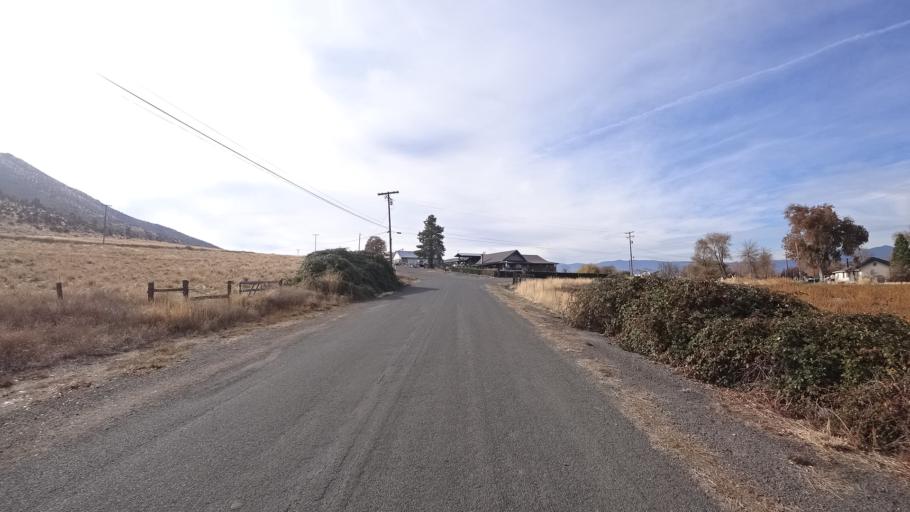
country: US
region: California
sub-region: Siskiyou County
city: Montague
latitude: 41.7206
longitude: -122.5209
